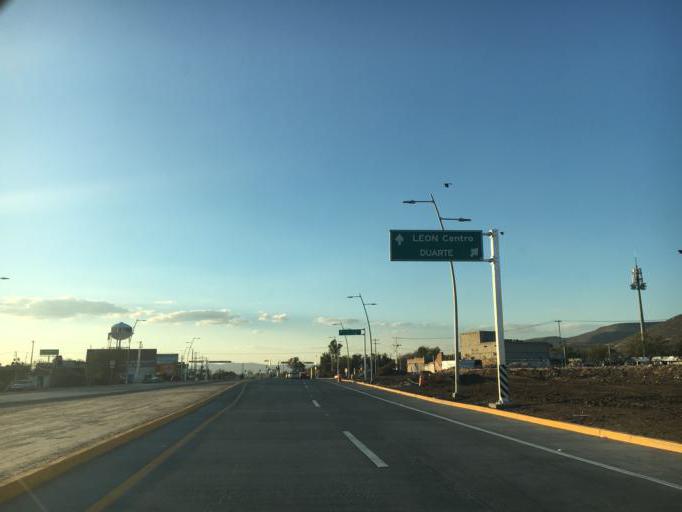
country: MX
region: Guanajuato
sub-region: Leon
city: Fraccionamiento Paraiso Real
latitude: 21.1050
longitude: -101.5788
